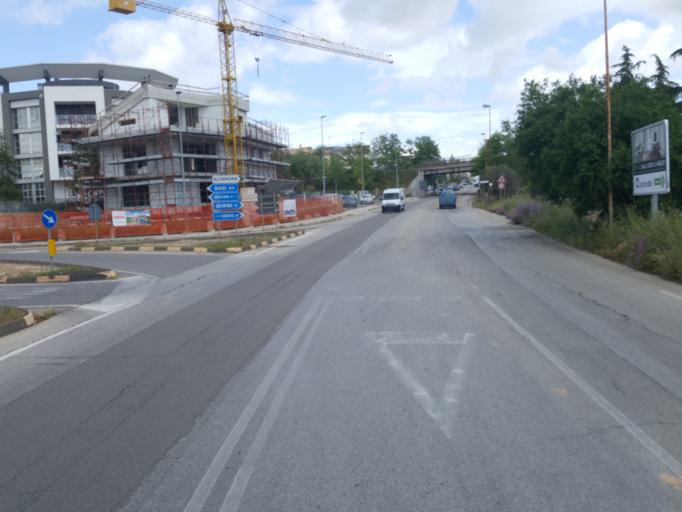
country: IT
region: Apulia
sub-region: Provincia di Bari
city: Altamura
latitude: 40.8137
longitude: 16.5540
